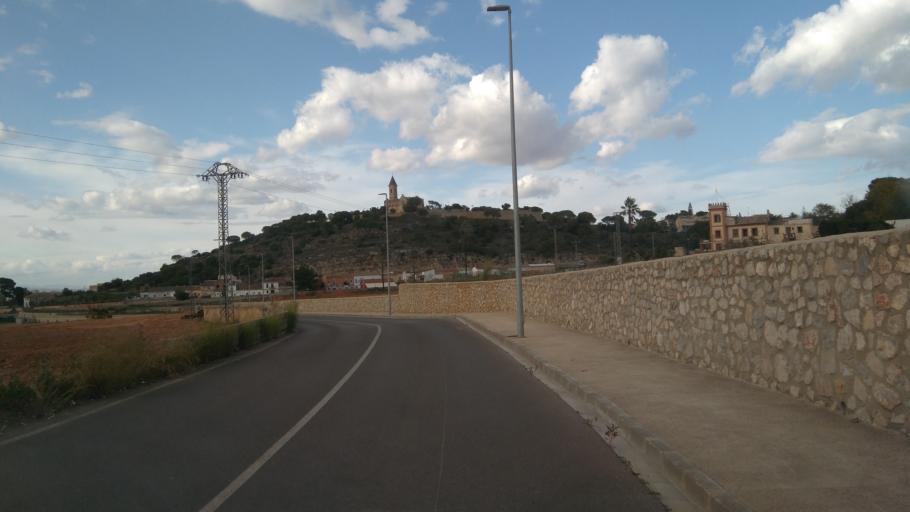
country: ES
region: Valencia
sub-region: Provincia de Valencia
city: Alzira
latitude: 39.1482
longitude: -0.4160
